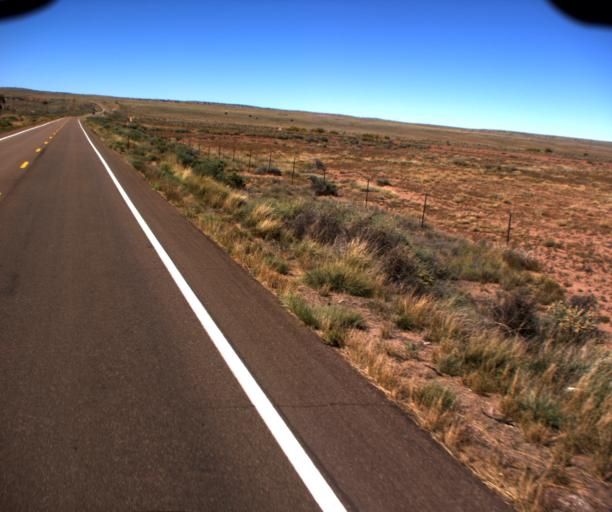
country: US
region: Arizona
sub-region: Apache County
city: Saint Johns
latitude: 34.5085
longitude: -109.4322
